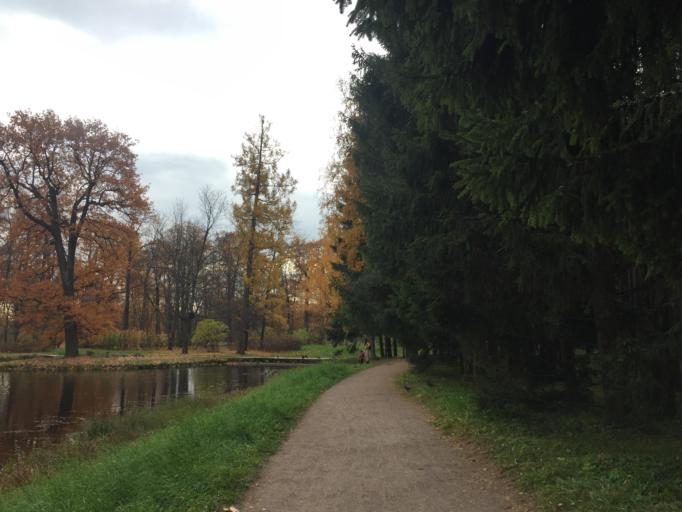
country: RU
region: St.-Petersburg
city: Pushkin
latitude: 59.7125
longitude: 30.3877
